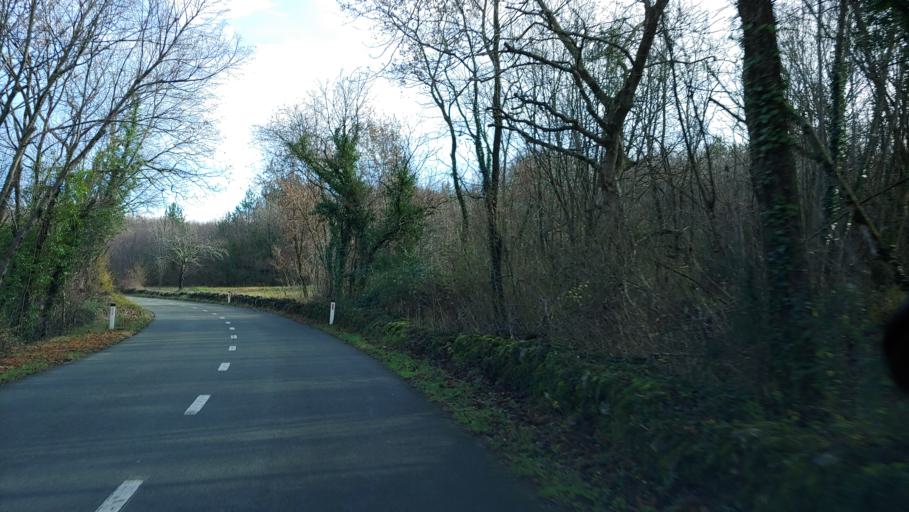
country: IT
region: Friuli Venezia Giulia
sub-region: Provincia di Trieste
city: Sistiana-Visogliano
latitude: 45.8104
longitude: 13.6471
